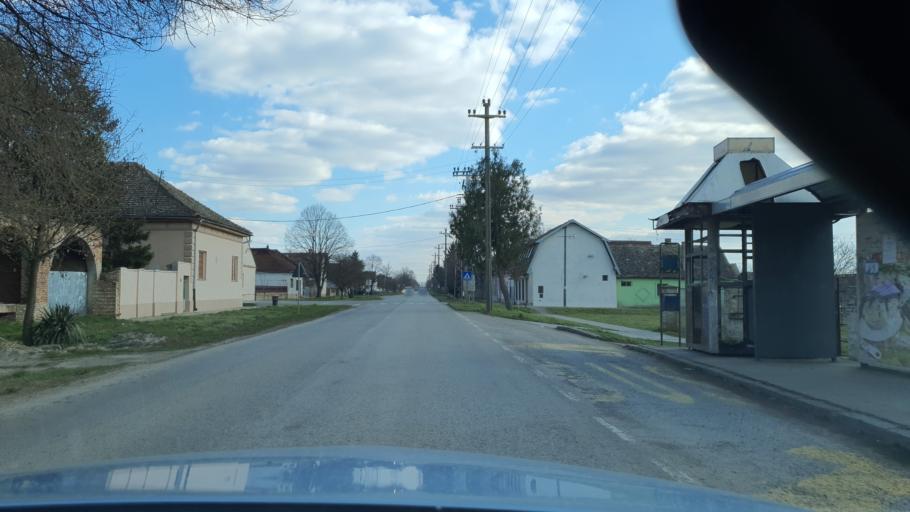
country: RS
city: Ravno Selo
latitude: 45.4487
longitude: 19.6213
